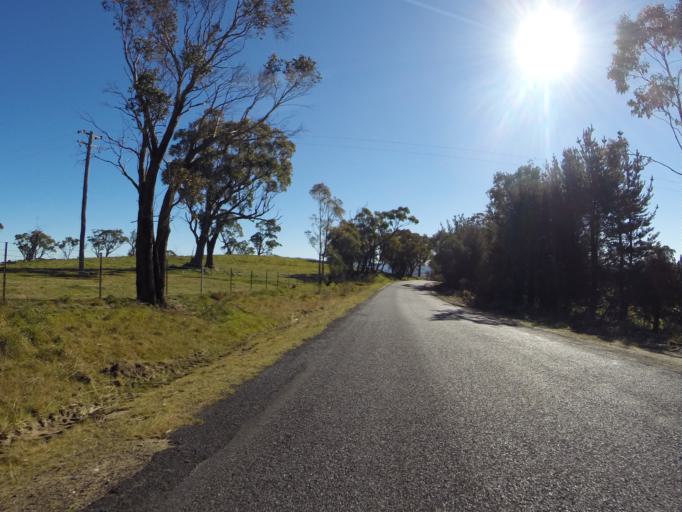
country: AU
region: New South Wales
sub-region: Oberon
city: Oberon
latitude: -33.5915
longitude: 149.8497
